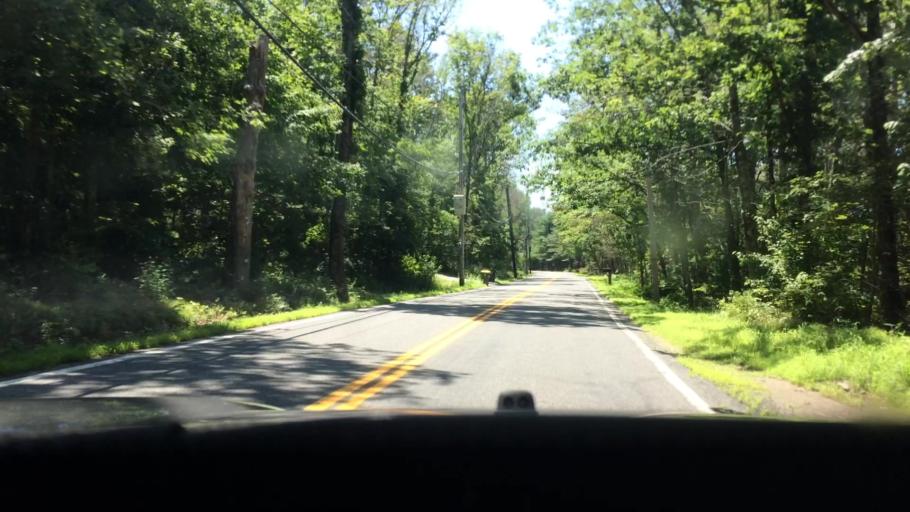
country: US
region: Rhode Island
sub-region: Providence County
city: Harrisville
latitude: 42.0018
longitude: -71.6812
